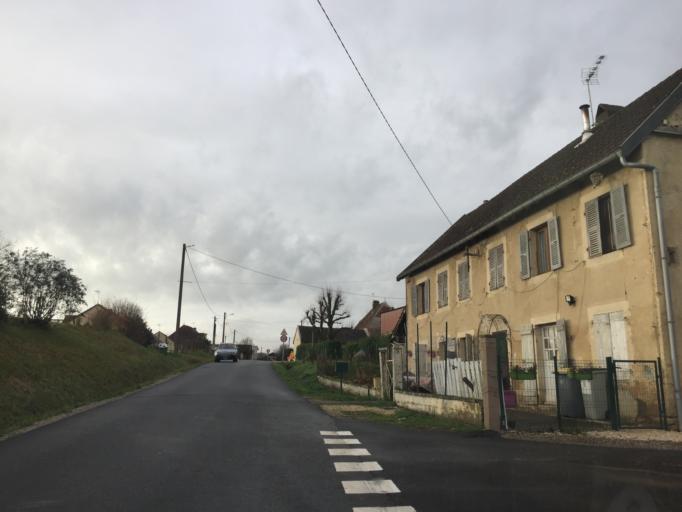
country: FR
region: Franche-Comte
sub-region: Departement du Jura
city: Mont-sous-Vaudrey
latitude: 46.9833
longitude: 5.5835
